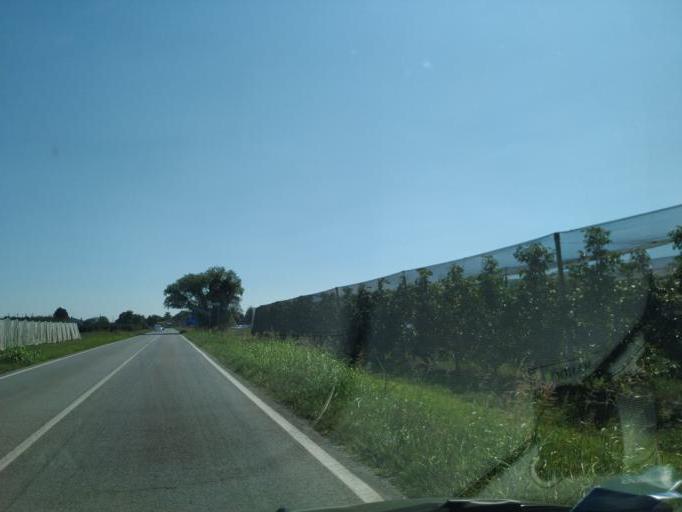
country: IT
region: Emilia-Romagna
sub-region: Provincia di Ferrara
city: La Saletta-Tamara
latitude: 44.8802
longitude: 11.7663
